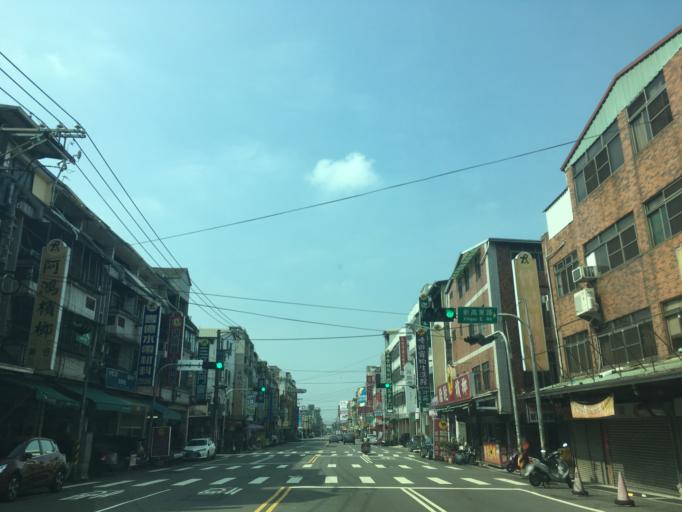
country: TW
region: Taiwan
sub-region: Taichung City
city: Taichung
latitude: 24.1530
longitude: 120.7114
